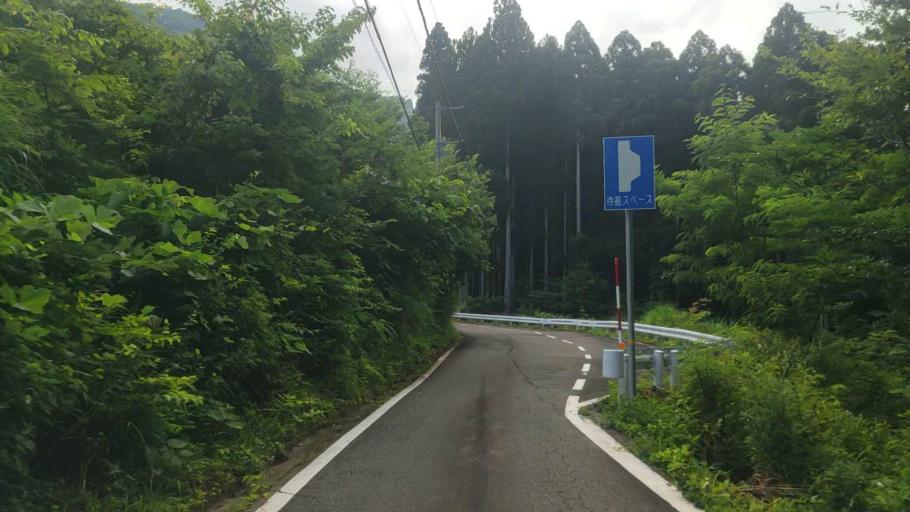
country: JP
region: Fukui
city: Katsuyama
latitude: 36.2245
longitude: 136.5313
